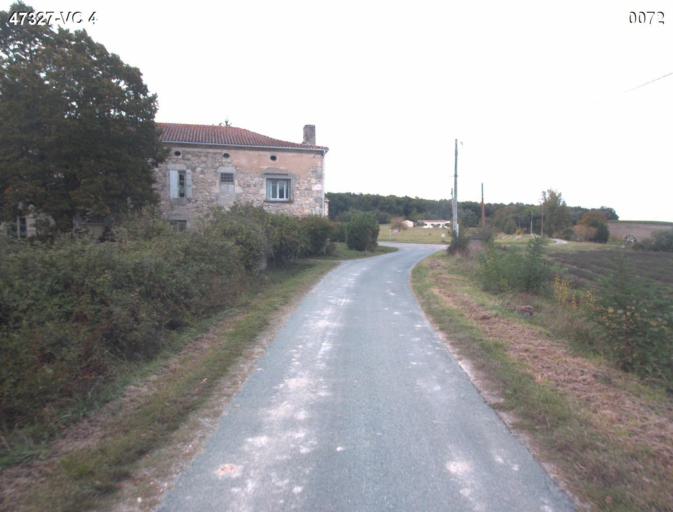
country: FR
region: Aquitaine
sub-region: Departement du Lot-et-Garonne
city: Barbaste
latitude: 44.2143
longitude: 0.2558
